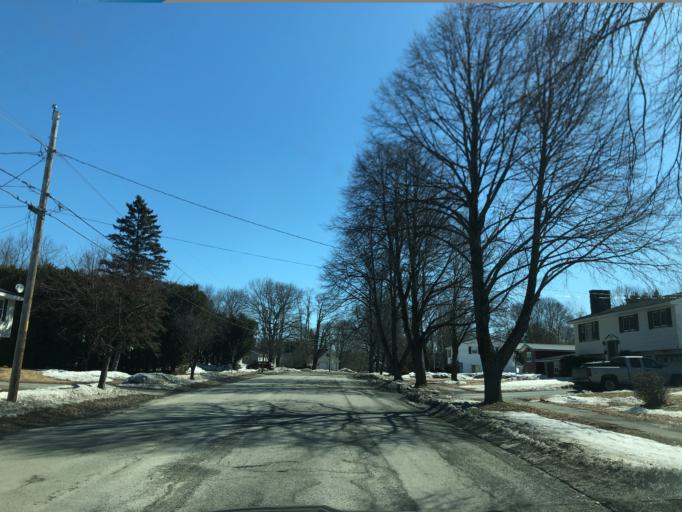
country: US
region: Maine
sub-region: Penobscot County
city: Brewer
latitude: 44.8180
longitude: -68.7566
